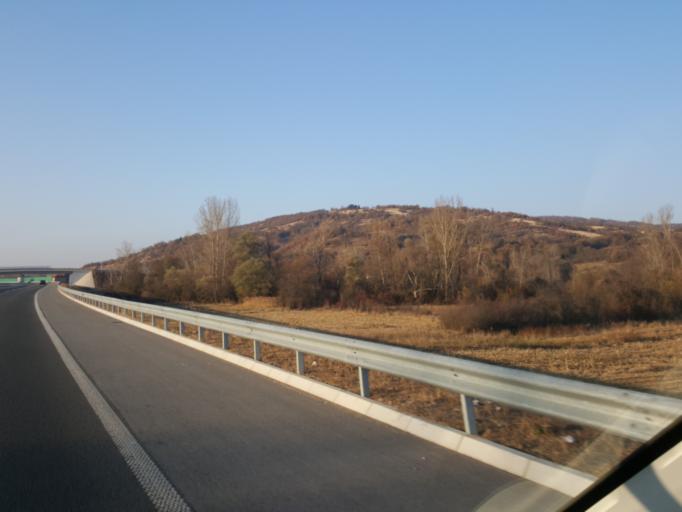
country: RS
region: Central Serbia
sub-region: Pirotski Okrug
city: Dimitrovgrad
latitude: 43.0420
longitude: 22.7093
